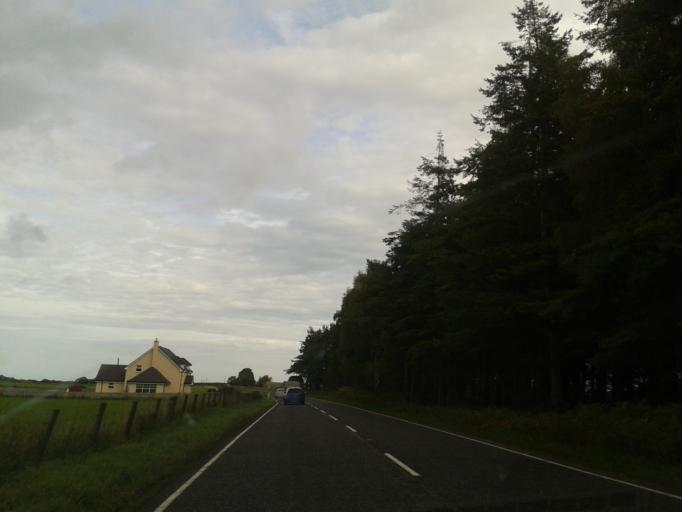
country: GB
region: Scotland
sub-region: Moray
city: Fochabers
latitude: 57.6303
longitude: -3.0410
